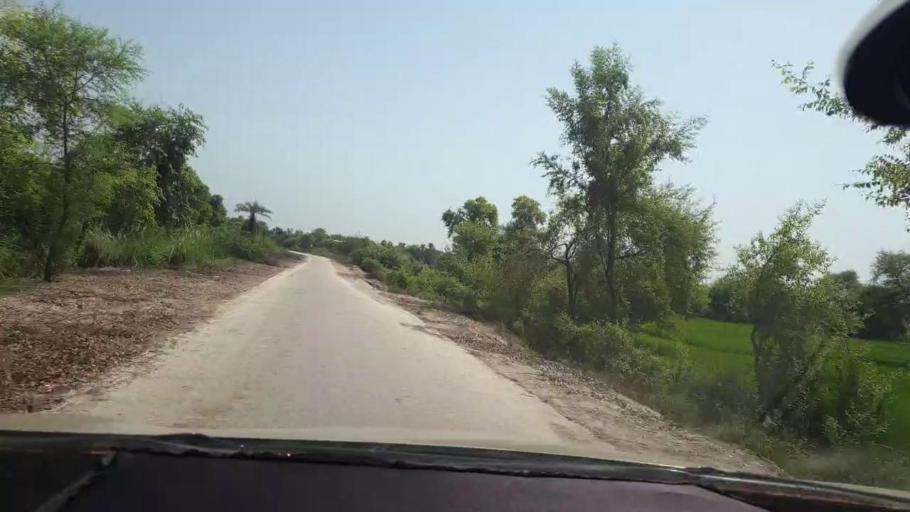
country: PK
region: Sindh
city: Kambar
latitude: 27.5111
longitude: 68.0119
